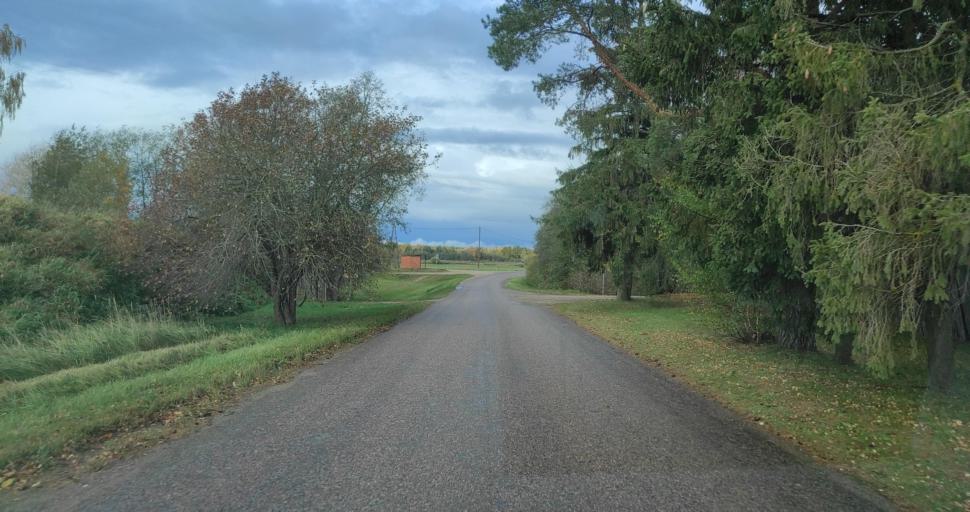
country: LV
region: Skrunda
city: Skrunda
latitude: 56.6085
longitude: 21.9795
